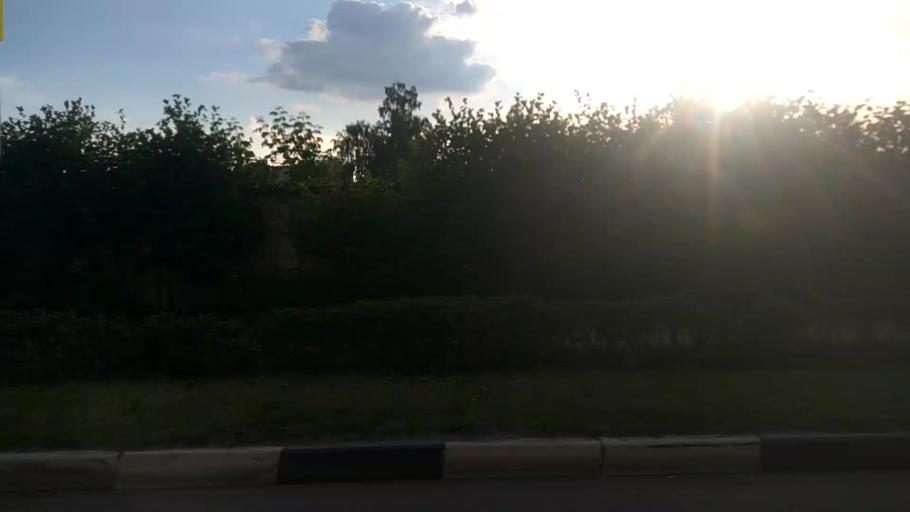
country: RU
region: Moskovskaya
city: Korolev
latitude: 55.9201
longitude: 37.7833
